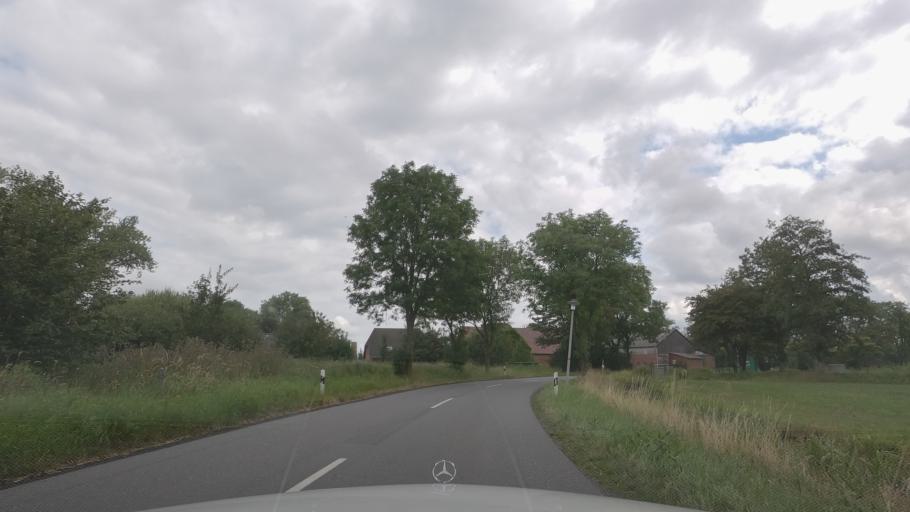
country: DE
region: Lower Saxony
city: Brake (Unterweser)
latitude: 53.3089
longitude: 8.5301
